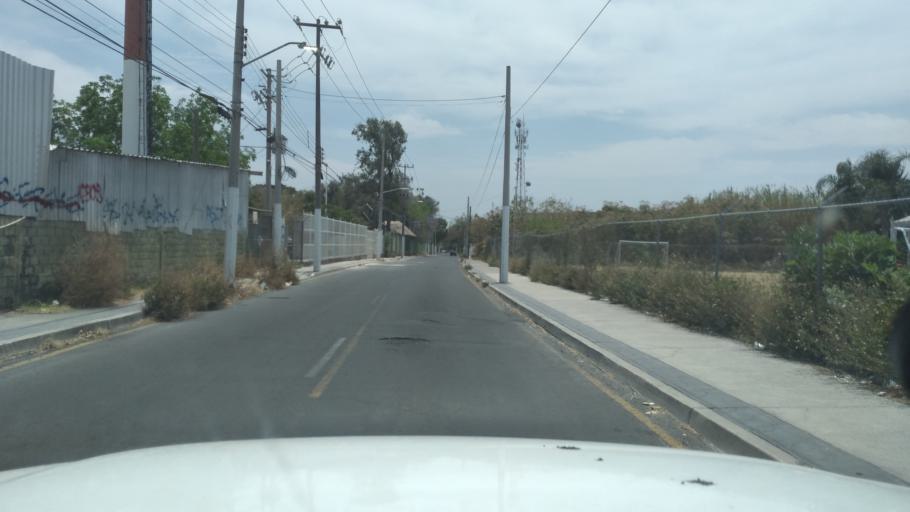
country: MX
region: Jalisco
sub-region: Zapopan
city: Zapopan
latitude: 20.7349
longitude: -103.3732
